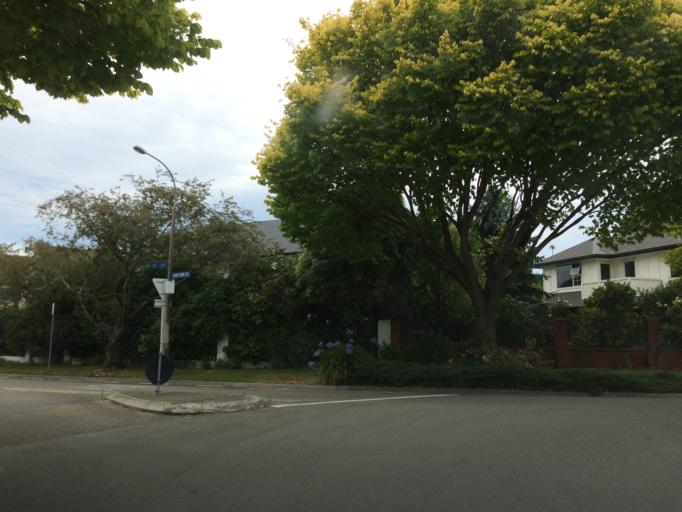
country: NZ
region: Canterbury
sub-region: Christchurch City
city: Christchurch
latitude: -43.5235
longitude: 172.5693
